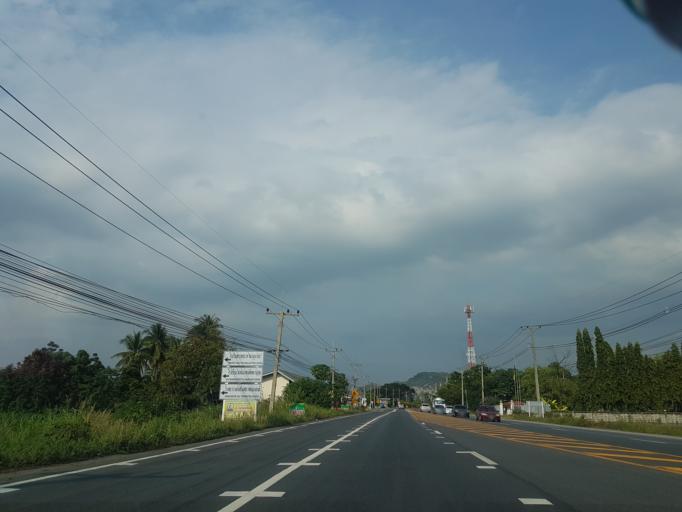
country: TH
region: Sara Buri
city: Nong Don
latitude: 14.6659
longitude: 100.7696
